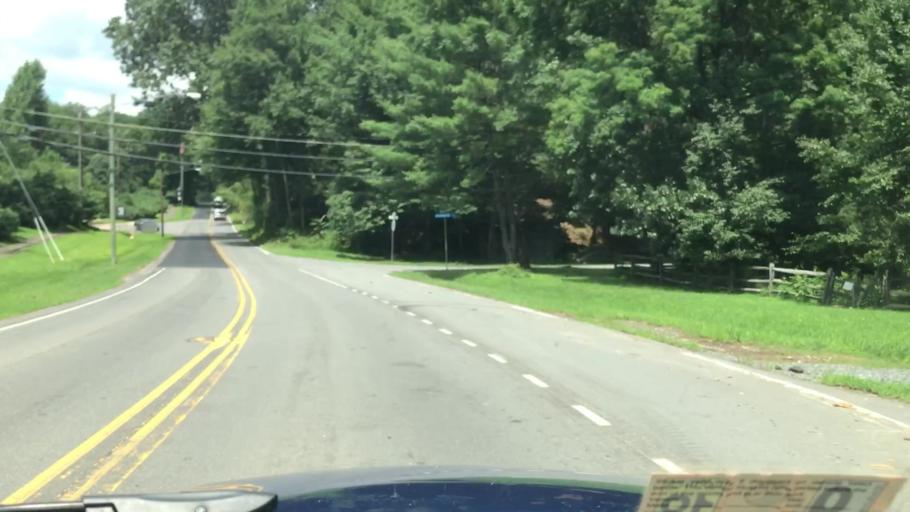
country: US
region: Virginia
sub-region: Fairfax County
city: Vienna
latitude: 38.9120
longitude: -77.2880
